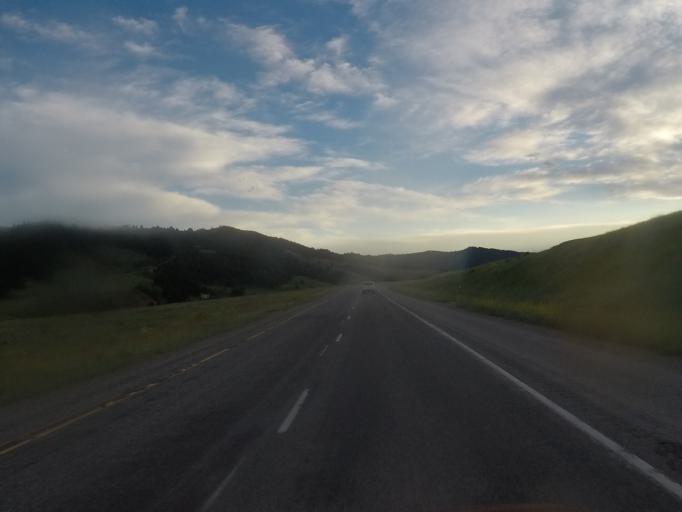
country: US
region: Montana
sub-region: Park County
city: Livingston
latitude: 45.6634
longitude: -110.7203
